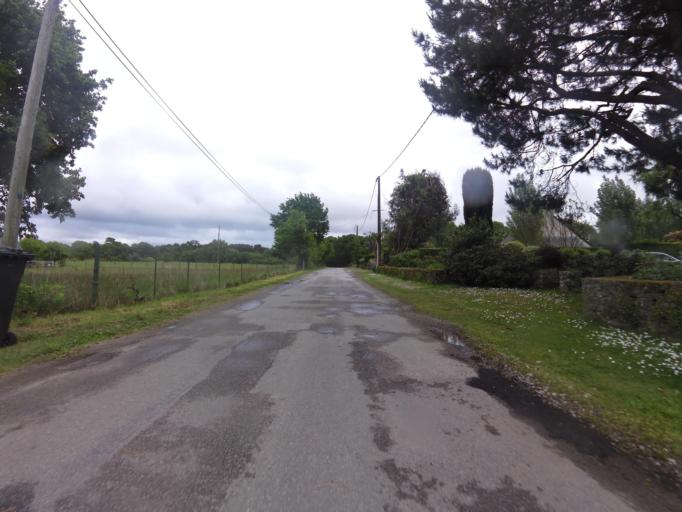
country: FR
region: Brittany
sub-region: Departement du Morbihan
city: Plougoumelen
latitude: 47.6356
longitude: -2.9102
